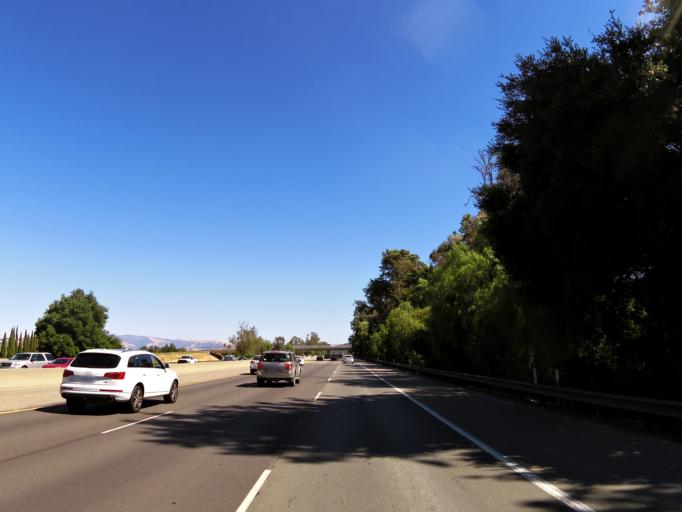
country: US
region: California
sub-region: Alameda County
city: Dublin
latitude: 37.6814
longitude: -121.9152
